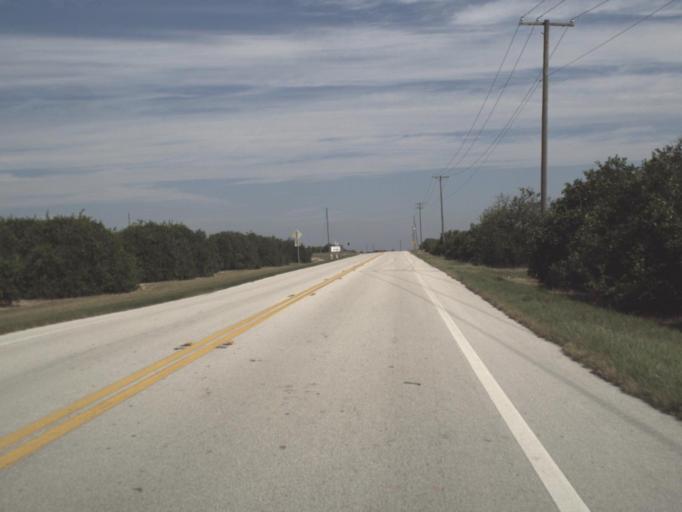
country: US
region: Florida
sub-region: Highlands County
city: Avon Park
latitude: 27.5734
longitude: -81.4654
